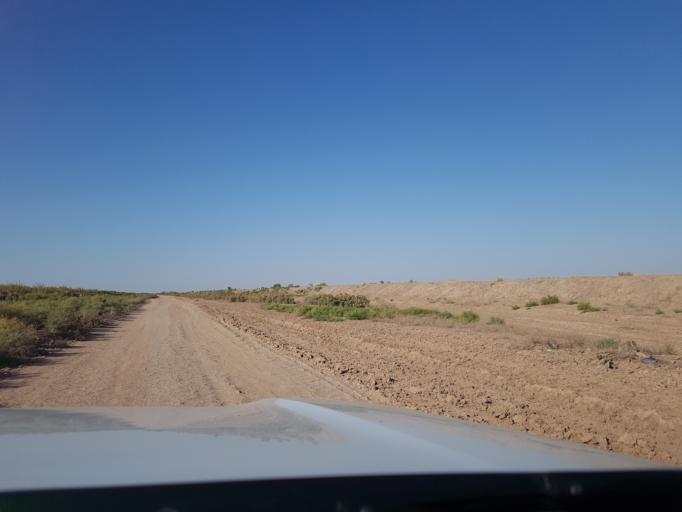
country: IR
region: Razavi Khorasan
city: Sarakhs
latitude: 36.9733
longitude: 61.3843
